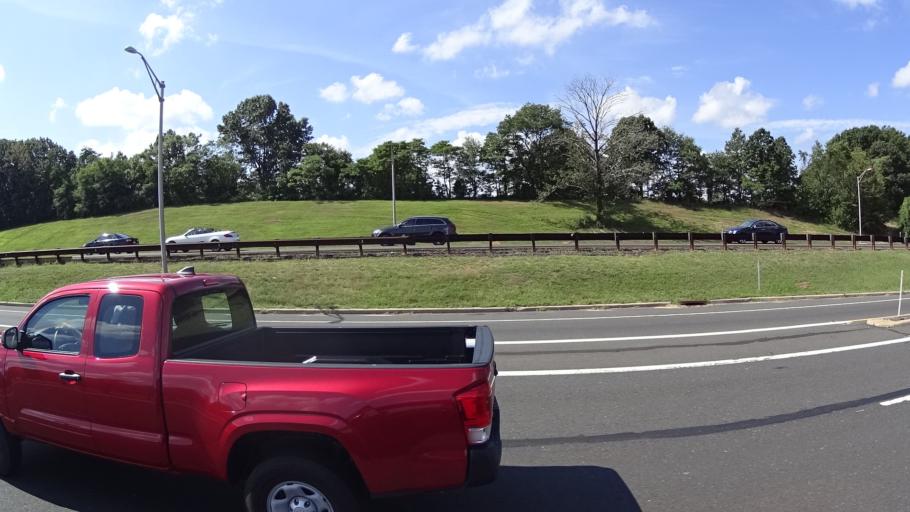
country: US
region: New Jersey
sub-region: Middlesex County
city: South Amboy
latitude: 40.4624
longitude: -74.2832
